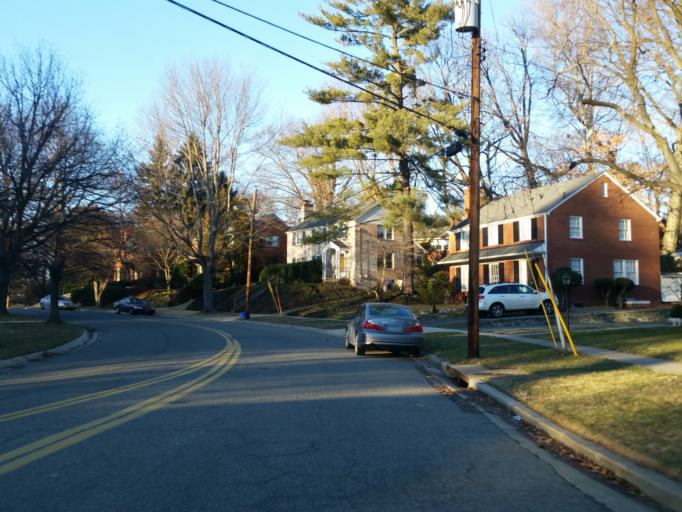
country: US
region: Maryland
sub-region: Montgomery County
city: Bethesda
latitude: 38.9704
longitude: -77.1203
